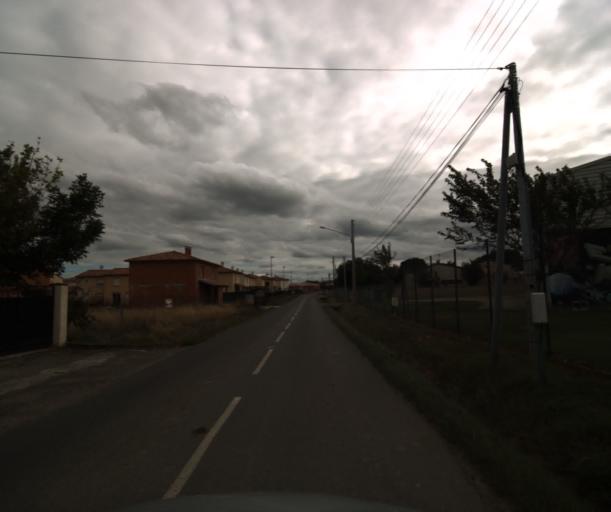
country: FR
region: Midi-Pyrenees
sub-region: Departement de la Haute-Garonne
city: Eaunes
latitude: 43.4351
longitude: 1.3625
